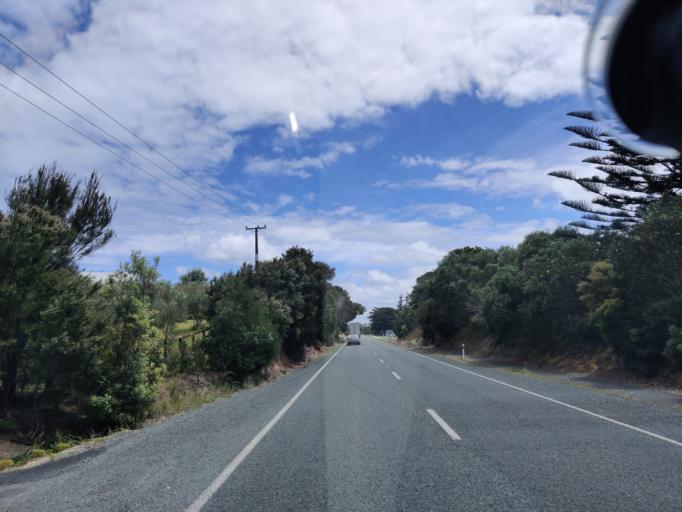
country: NZ
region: Northland
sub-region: Far North District
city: Kaitaia
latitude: -34.8320
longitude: 173.1299
